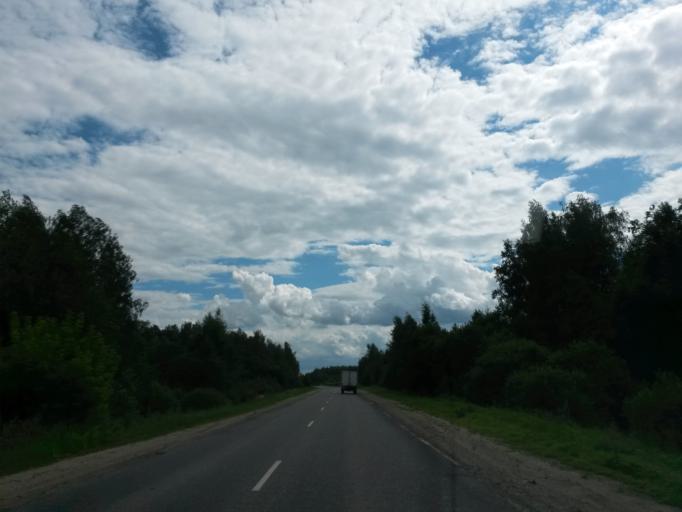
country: RU
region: Ivanovo
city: Novo-Talitsy
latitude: 57.0369
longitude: 40.7458
